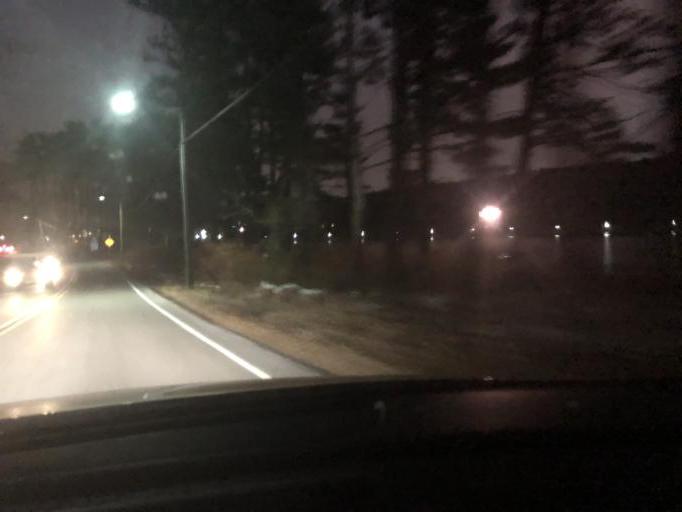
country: US
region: New Jersey
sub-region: Essex County
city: South Orange
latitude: 40.7623
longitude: -74.2887
